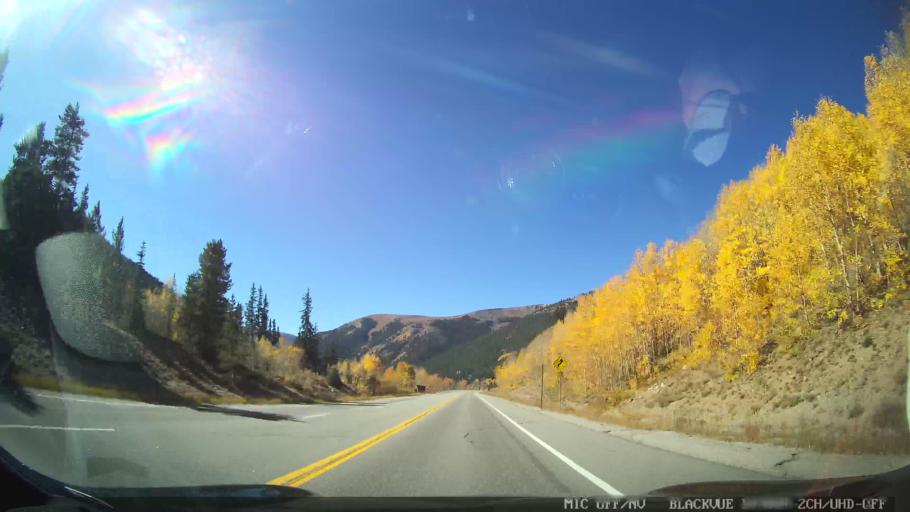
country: US
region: Colorado
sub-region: Lake County
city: Leadville
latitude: 39.3567
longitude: -106.2110
